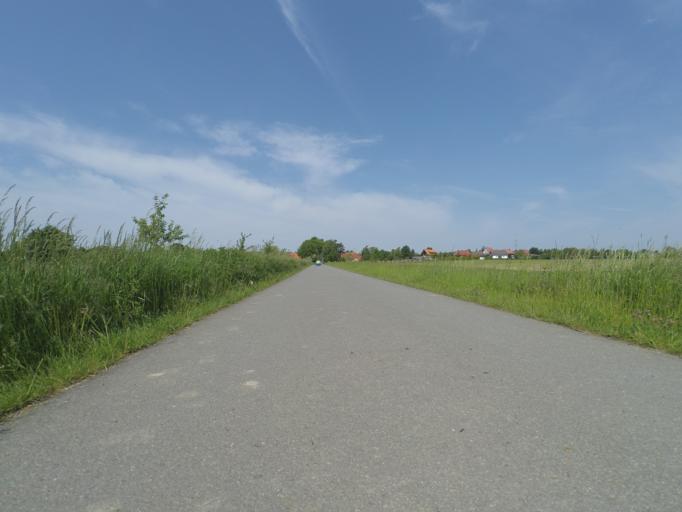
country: DE
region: Lower Saxony
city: Algermissen
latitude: 52.2827
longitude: 9.9812
